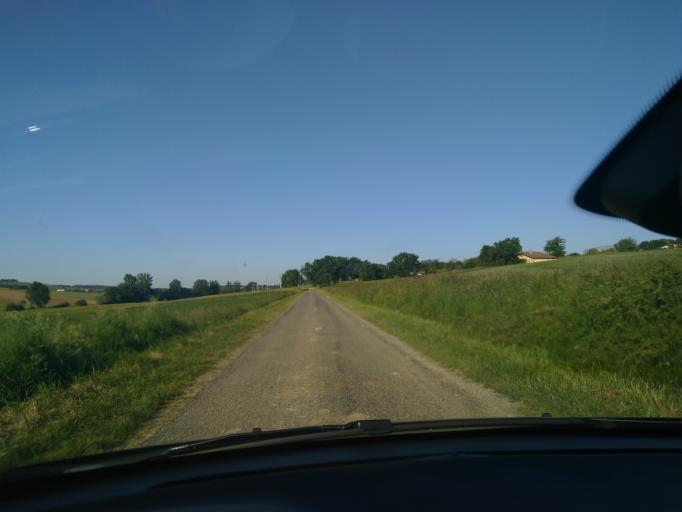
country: FR
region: Midi-Pyrenees
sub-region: Departement du Tarn-et-Garonne
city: Beaumont-de-Lomagne
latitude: 43.8233
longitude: 1.0525
